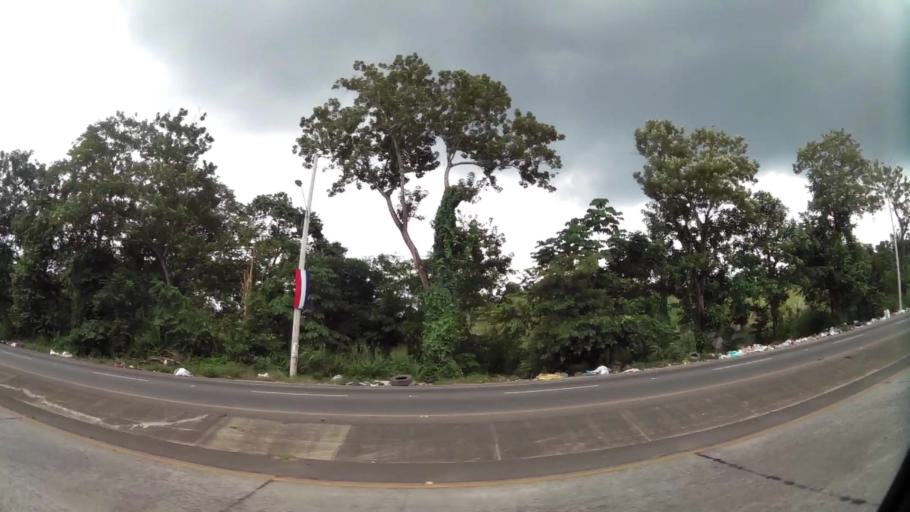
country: PA
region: Panama
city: Cabra Numero Uno
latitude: 9.1007
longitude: -79.3351
